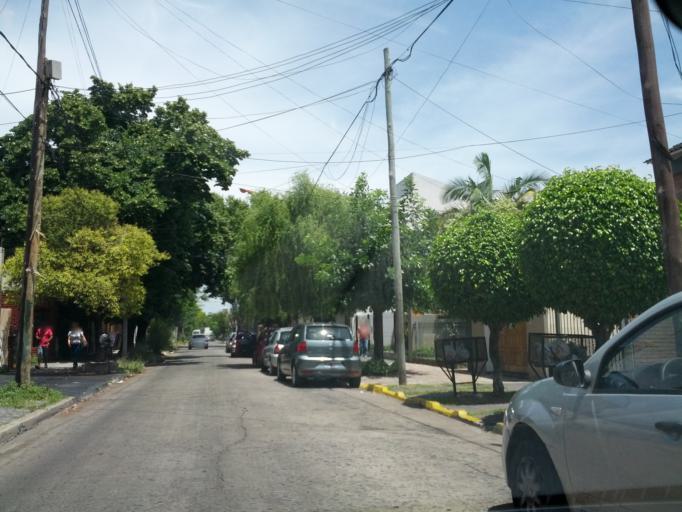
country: AR
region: Buenos Aires
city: San Justo
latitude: -34.6485
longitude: -58.5678
